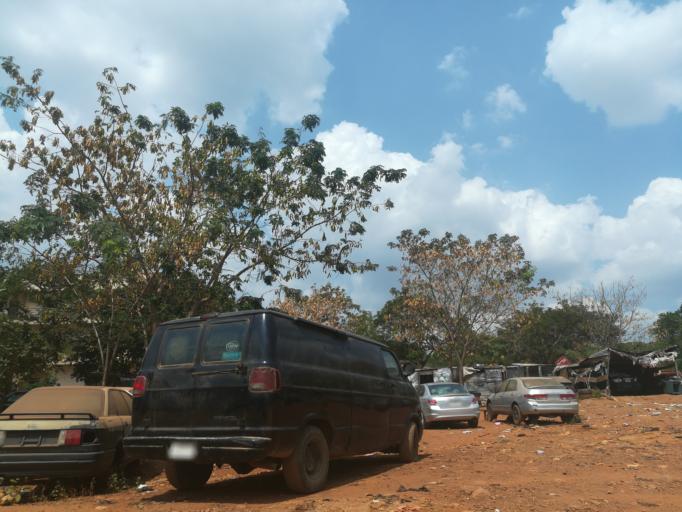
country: NG
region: Abuja Federal Capital Territory
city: Abuja
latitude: 9.0594
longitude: 7.4502
